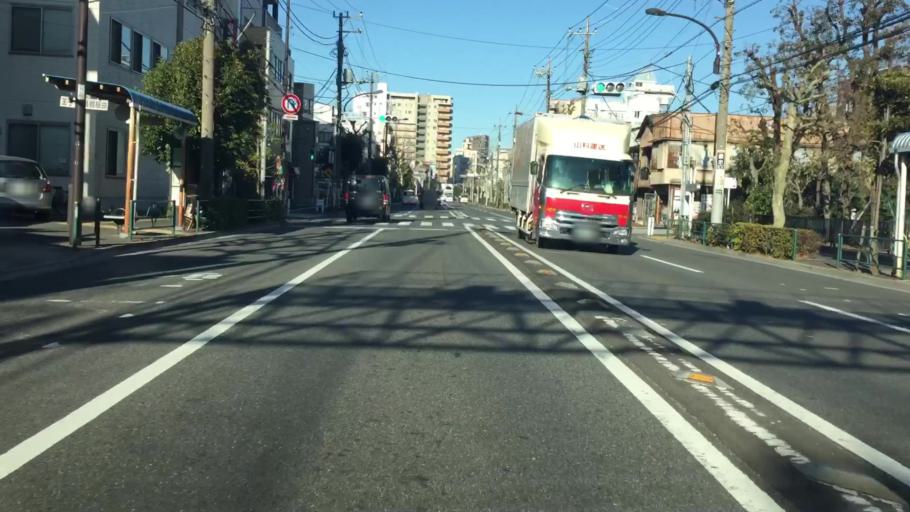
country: JP
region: Saitama
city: Kawaguchi
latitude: 35.7491
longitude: 139.7512
